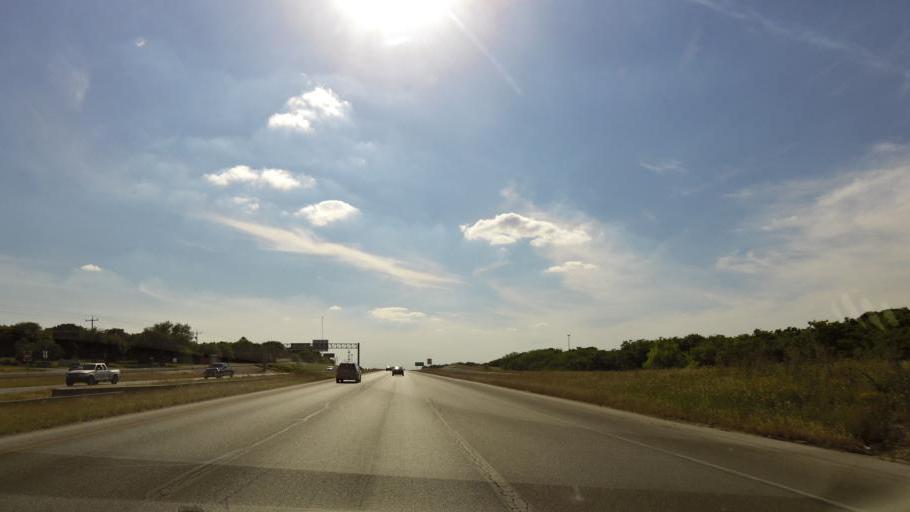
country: US
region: Texas
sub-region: Bexar County
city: Live Oak
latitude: 29.6028
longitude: -98.3728
